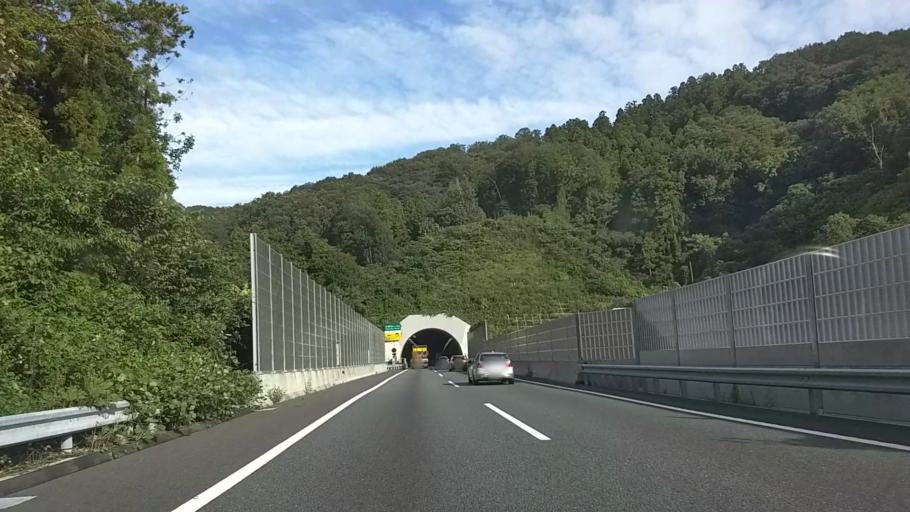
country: JP
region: Tokyo
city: Hachioji
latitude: 35.5589
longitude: 139.3127
